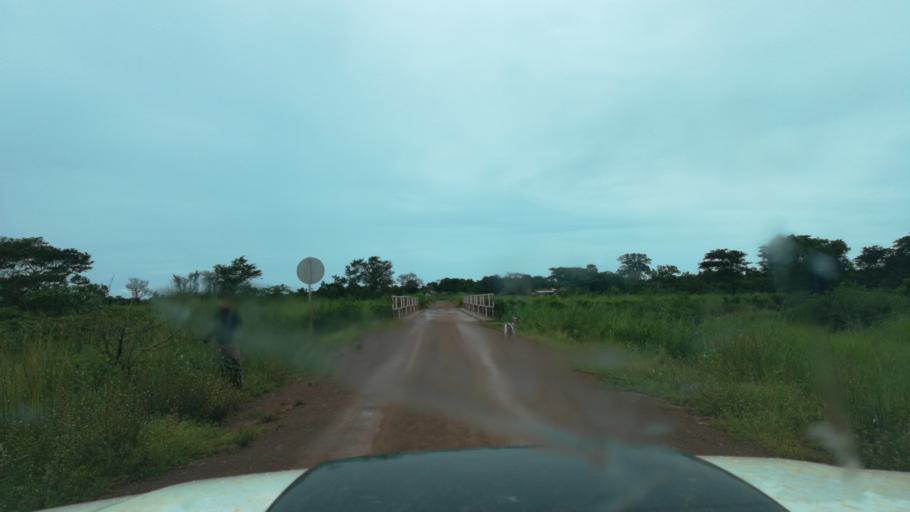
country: ZM
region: Luapula
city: Mwense
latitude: -10.1798
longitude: 28.1234
